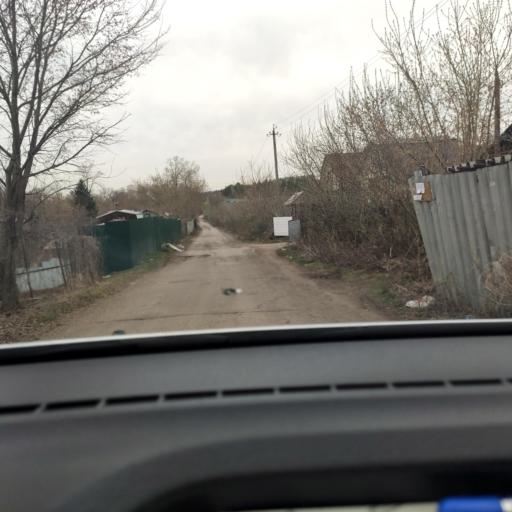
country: RU
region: Bashkortostan
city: Avdon
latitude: 54.6240
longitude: 55.5980
